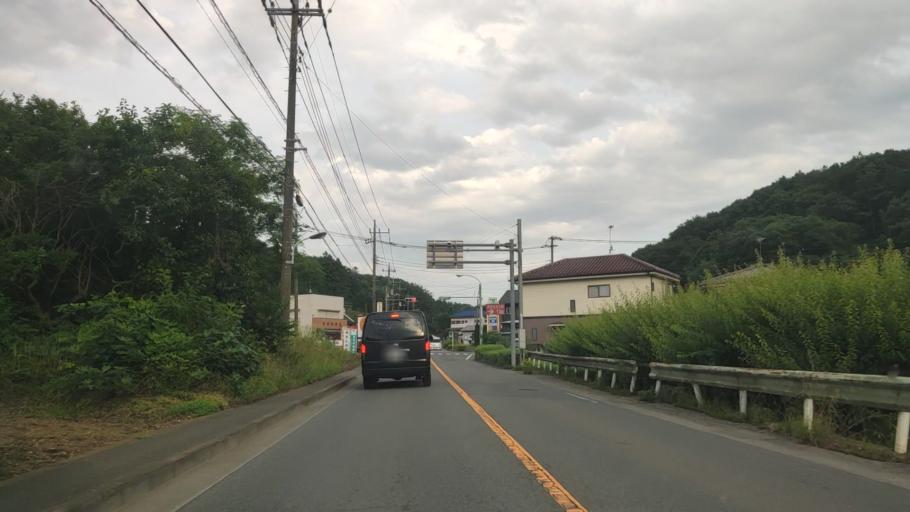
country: JP
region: Saitama
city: Hanno
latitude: 35.8206
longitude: 139.2917
